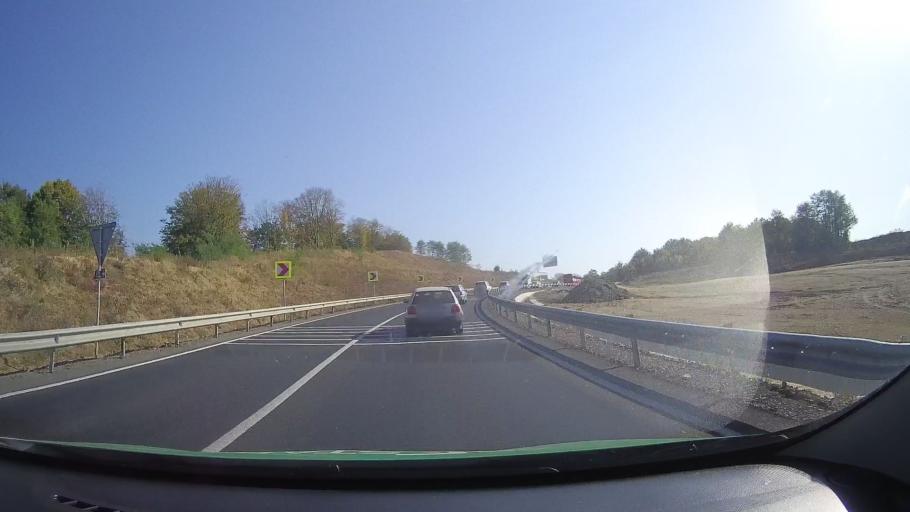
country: RO
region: Timis
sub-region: Comuna Pietroasa
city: Pietroasa
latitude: 45.8871
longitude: 22.4048
